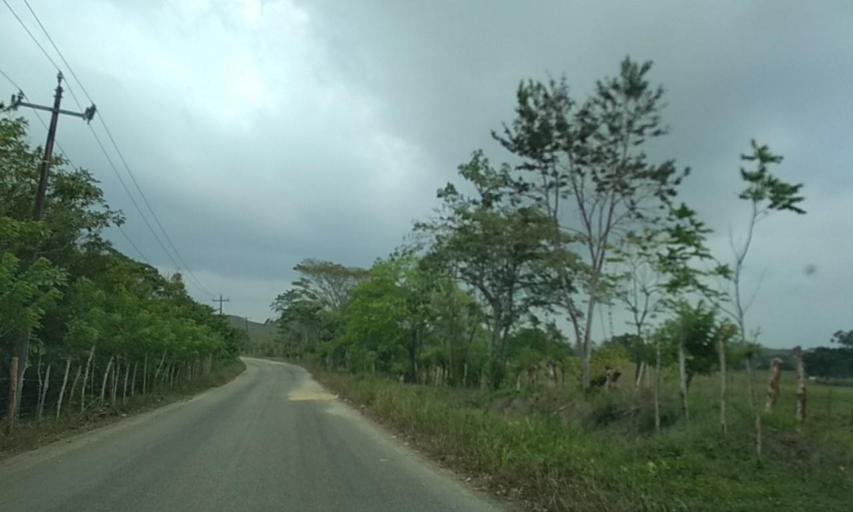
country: MX
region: Tabasco
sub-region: Huimanguillo
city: Francisco Rueda
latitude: 17.6049
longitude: -94.0931
